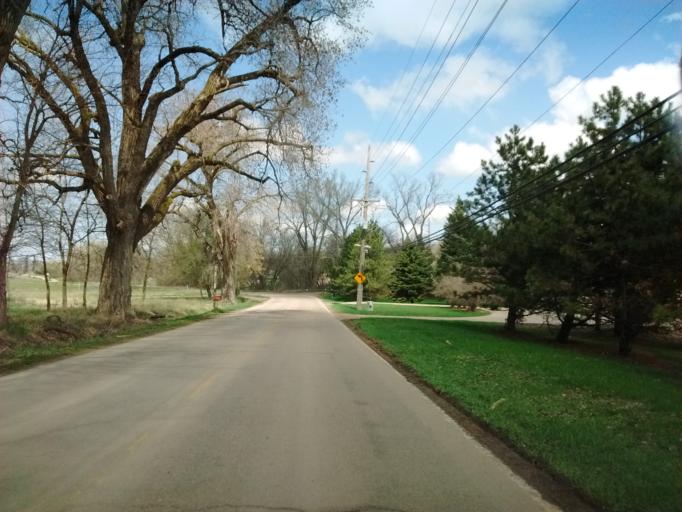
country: US
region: Iowa
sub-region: Woodbury County
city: Sioux City
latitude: 42.5405
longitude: -96.4302
